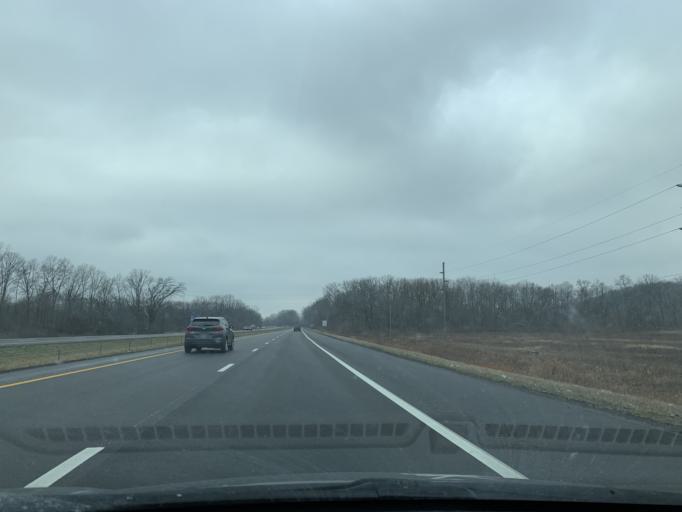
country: US
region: Ohio
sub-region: Licking County
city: Granville South
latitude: 40.0637
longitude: -82.5387
